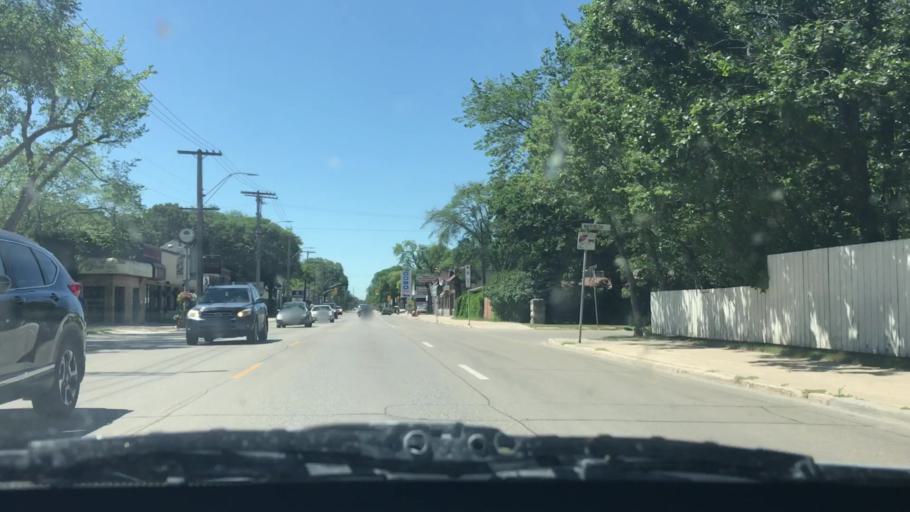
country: CA
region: Manitoba
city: Winnipeg
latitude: 49.8738
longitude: -97.1833
